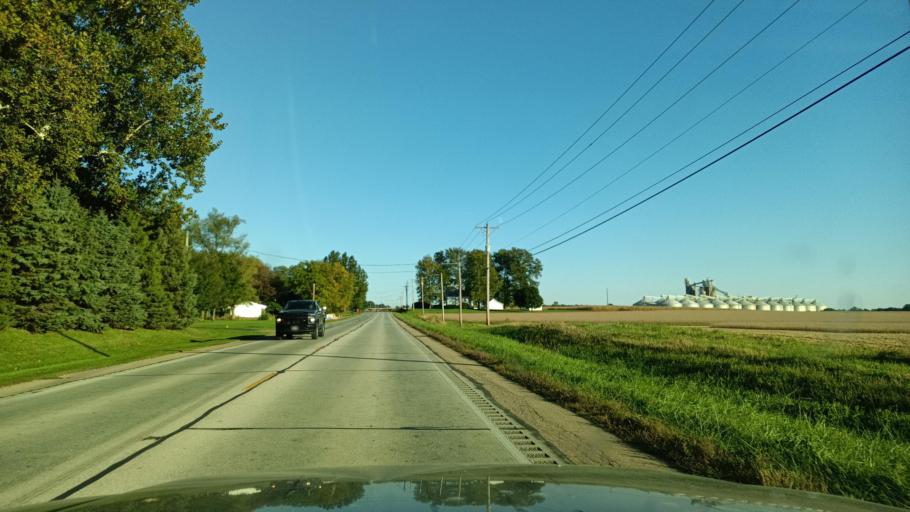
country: US
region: Illinois
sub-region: Champaign County
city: Lake of the Woods
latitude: 40.1674
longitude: -88.3298
